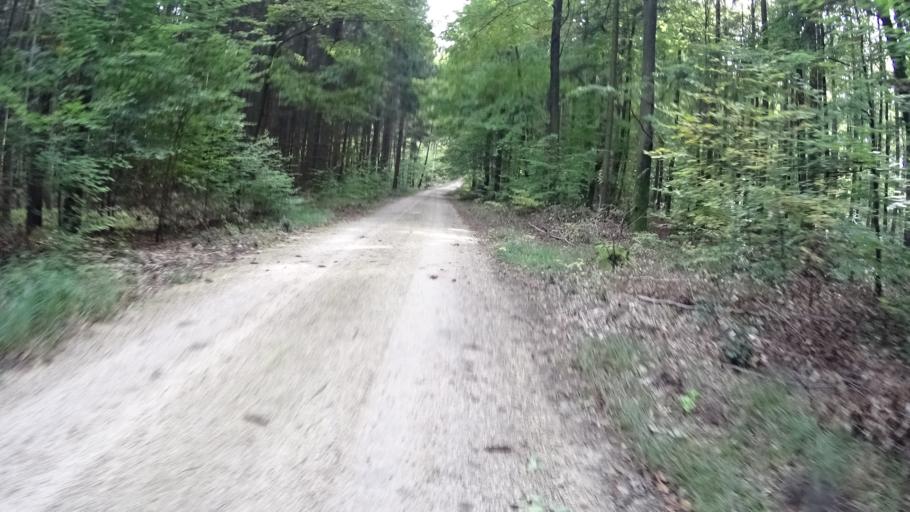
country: DE
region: Bavaria
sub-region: Upper Bavaria
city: Walting
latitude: 48.9110
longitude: 11.3249
